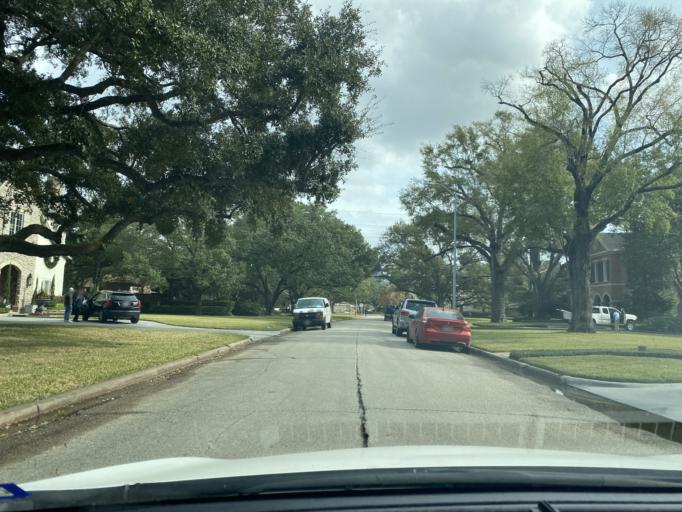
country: US
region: Texas
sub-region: Harris County
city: Hunters Creek Village
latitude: 29.7546
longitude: -95.4753
